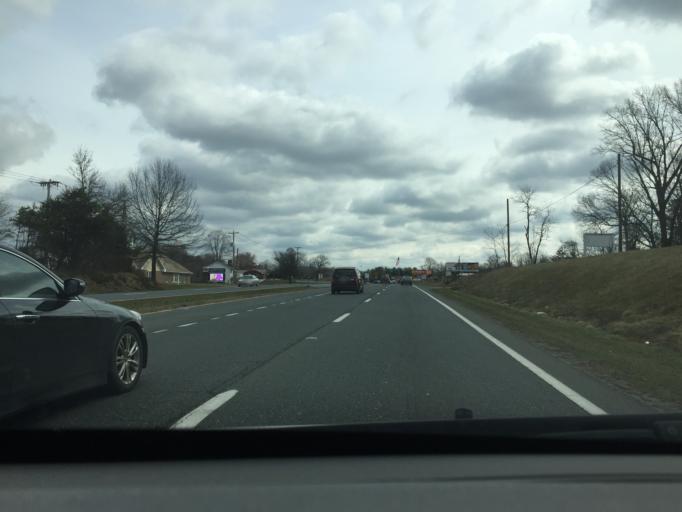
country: US
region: Virginia
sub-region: Campbell County
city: Timberlake
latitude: 37.3053
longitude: -79.2774
